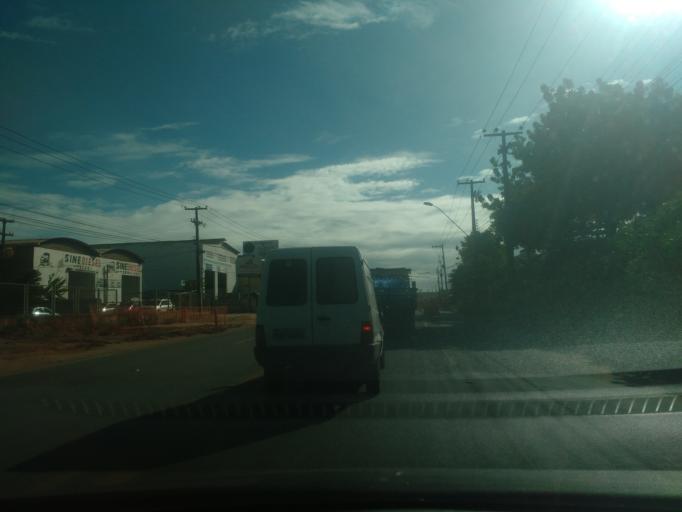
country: BR
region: Alagoas
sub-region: Satuba
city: Satuba
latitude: -9.5638
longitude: -35.7728
